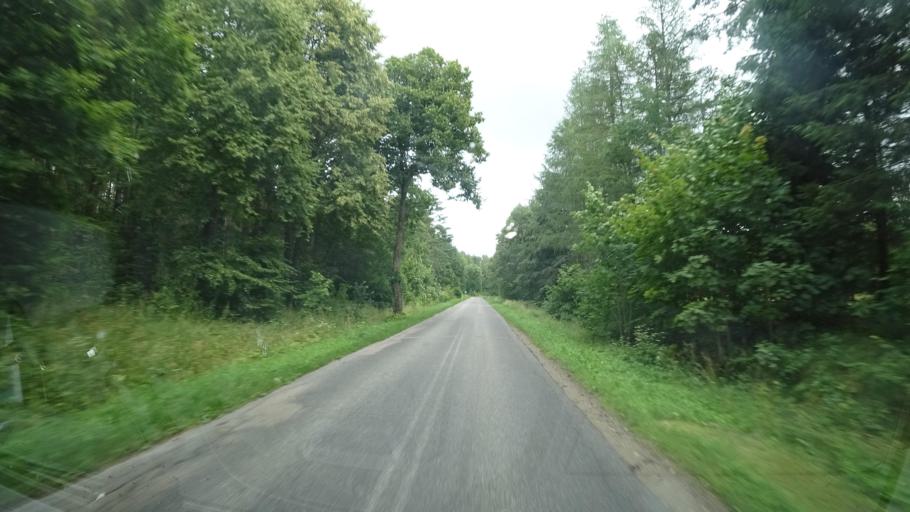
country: PL
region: Warmian-Masurian Voivodeship
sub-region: Powiat goldapski
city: Goldap
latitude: 54.3102
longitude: 22.3786
